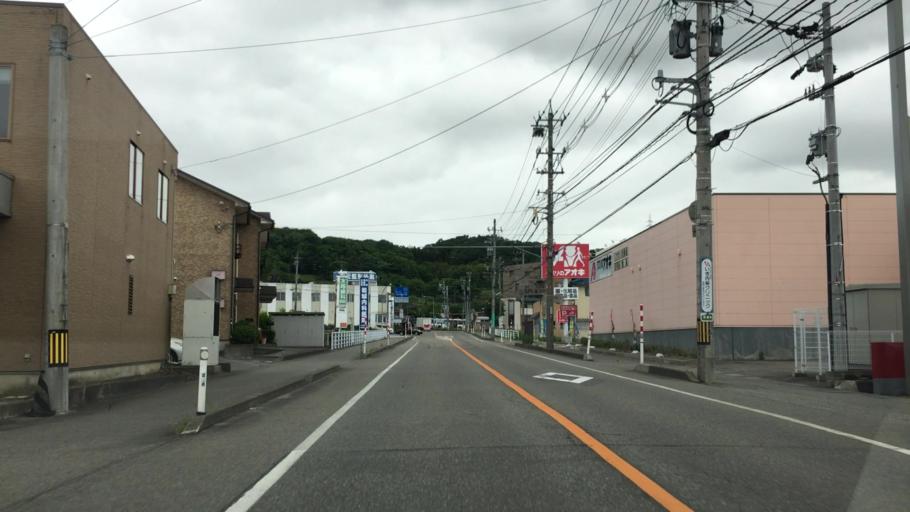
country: JP
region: Toyama
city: Toyama-shi
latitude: 36.7092
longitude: 137.1791
